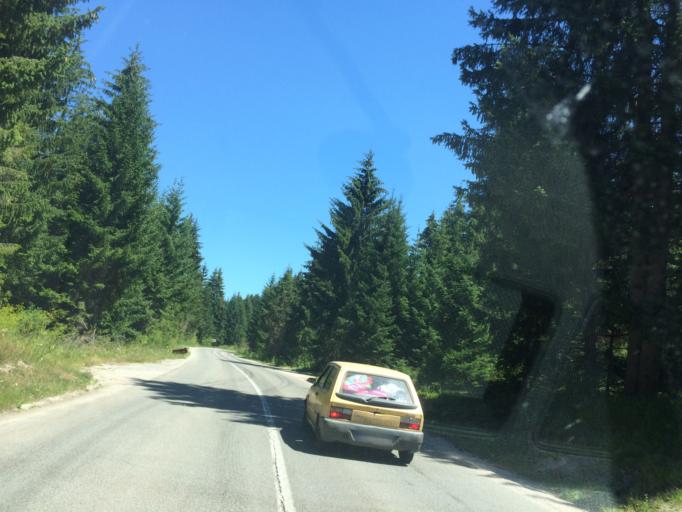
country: ME
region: Pljevlja
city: Pljevlja
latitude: 43.3446
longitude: 19.5016
